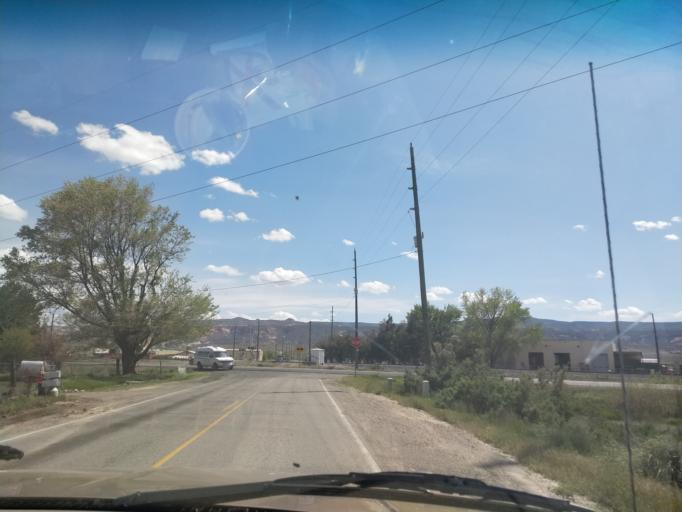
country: US
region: Colorado
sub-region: Mesa County
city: Fruita
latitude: 39.1682
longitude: -108.7571
